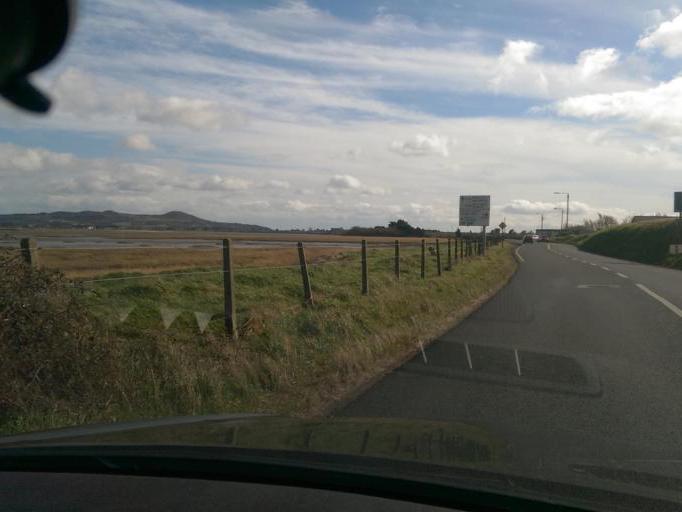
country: IE
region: Leinster
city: Portmarnock
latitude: 53.4110
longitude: -6.1370
